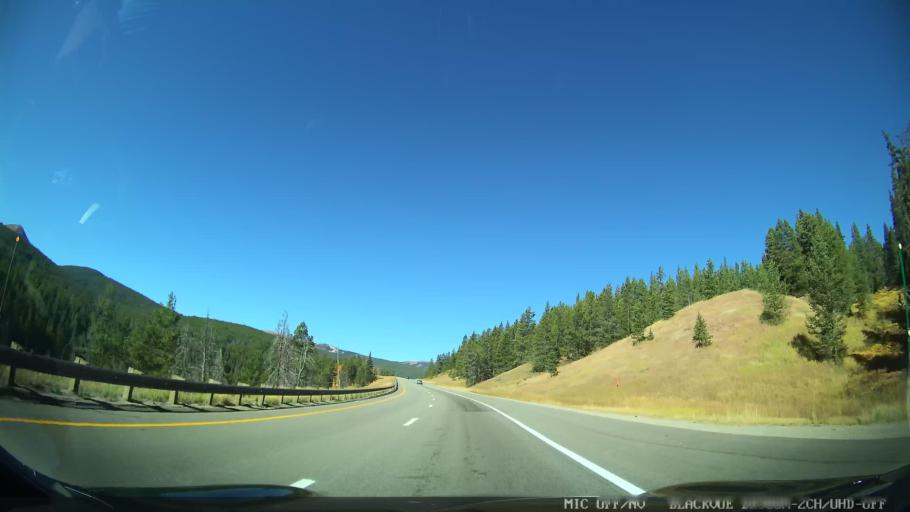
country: US
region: Colorado
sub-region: Summit County
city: Frisco
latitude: 39.5037
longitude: -106.1728
